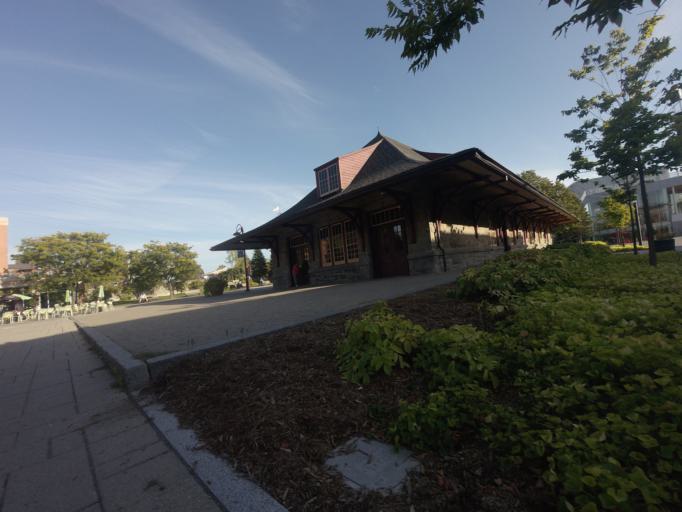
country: CA
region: Quebec
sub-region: Laurentides
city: Saint-Jerome
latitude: 45.7769
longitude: -74.0006
